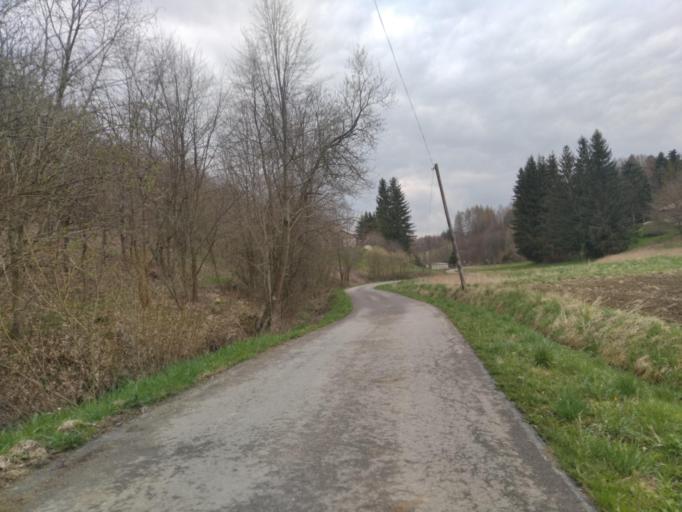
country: PL
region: Subcarpathian Voivodeship
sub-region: Powiat strzyzowski
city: Wisniowa
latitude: 49.8946
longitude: 21.7125
